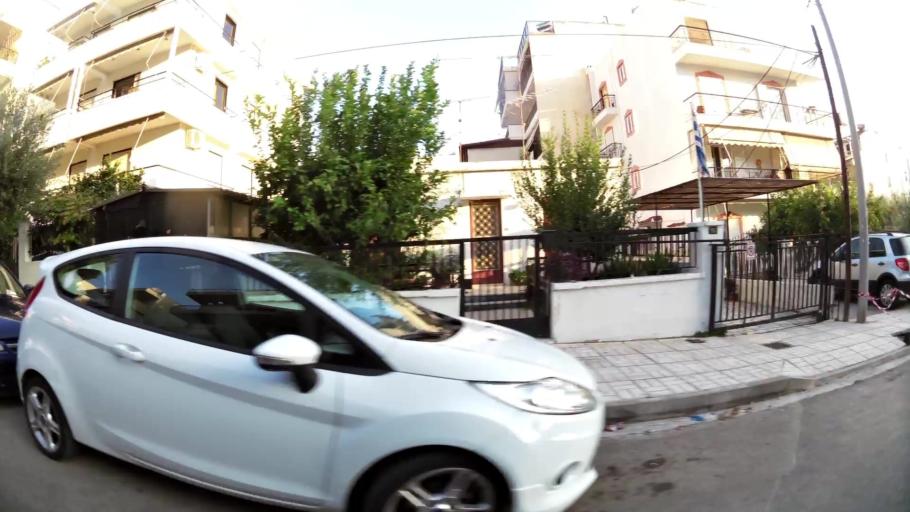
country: GR
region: Attica
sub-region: Nomarchia Athinas
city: Argyroupoli
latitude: 37.8964
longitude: 23.7696
